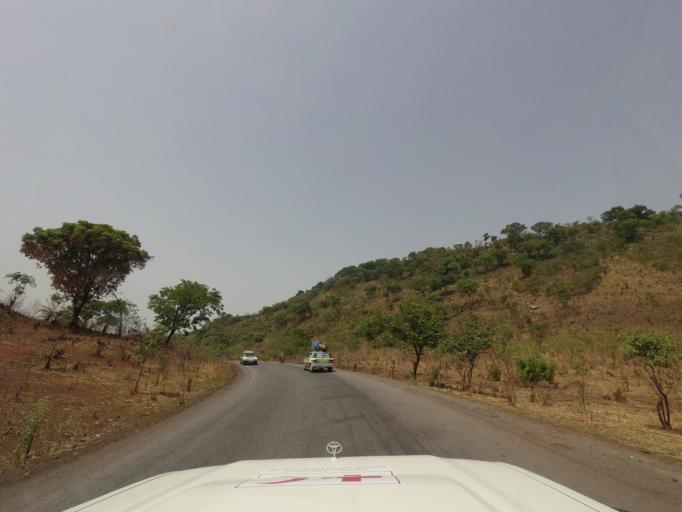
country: GN
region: Mamou
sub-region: Mamou Prefecture
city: Mamou
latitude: 10.2043
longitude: -12.4666
